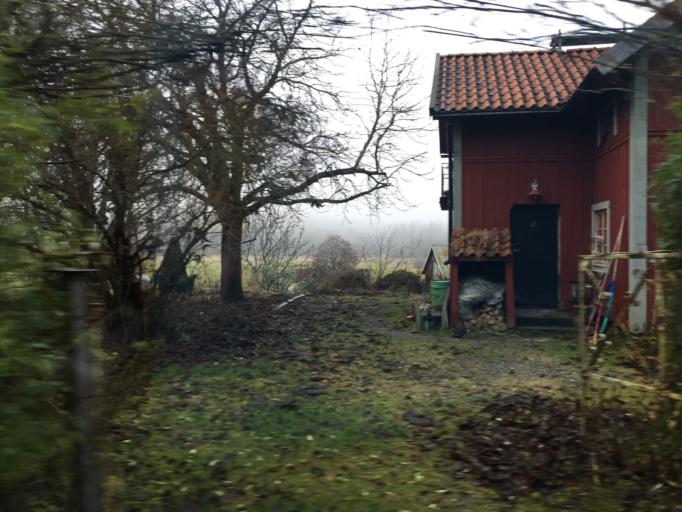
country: SE
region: Stockholm
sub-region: Nynashamns Kommun
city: Osmo
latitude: 59.0480
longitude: 17.8898
